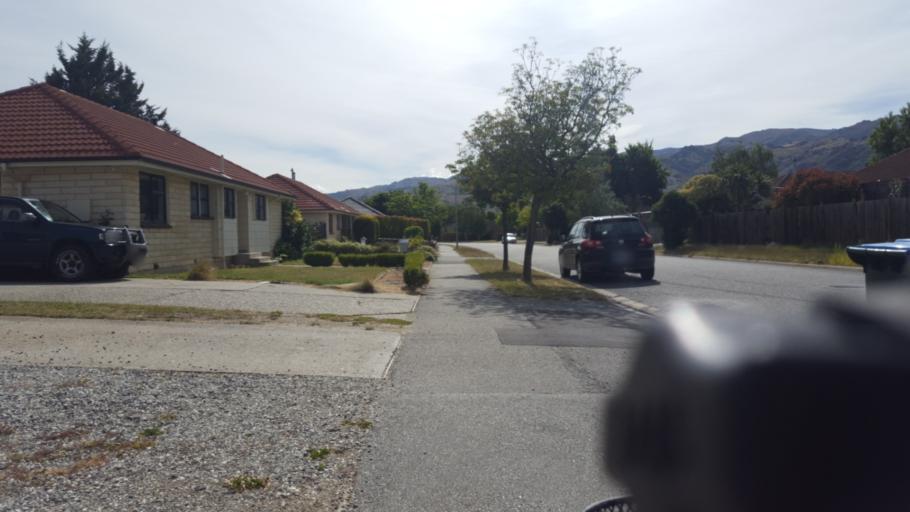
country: NZ
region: Otago
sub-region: Queenstown-Lakes District
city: Wanaka
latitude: -45.0420
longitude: 169.1896
